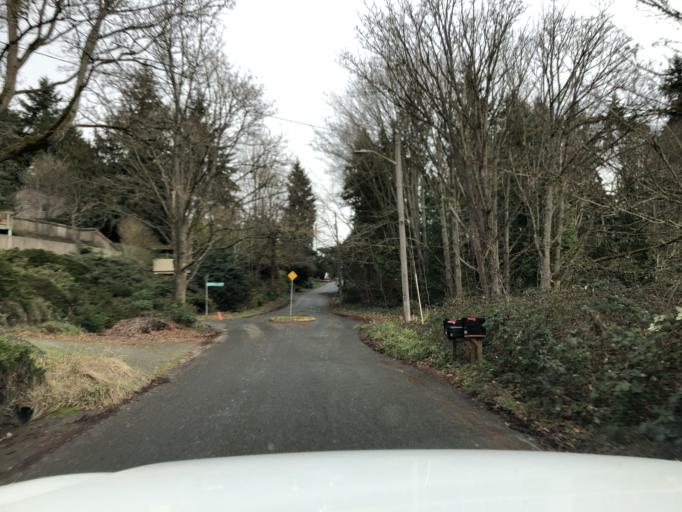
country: US
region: Washington
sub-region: King County
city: Inglewood-Finn Hill
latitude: 47.7047
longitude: -122.2804
